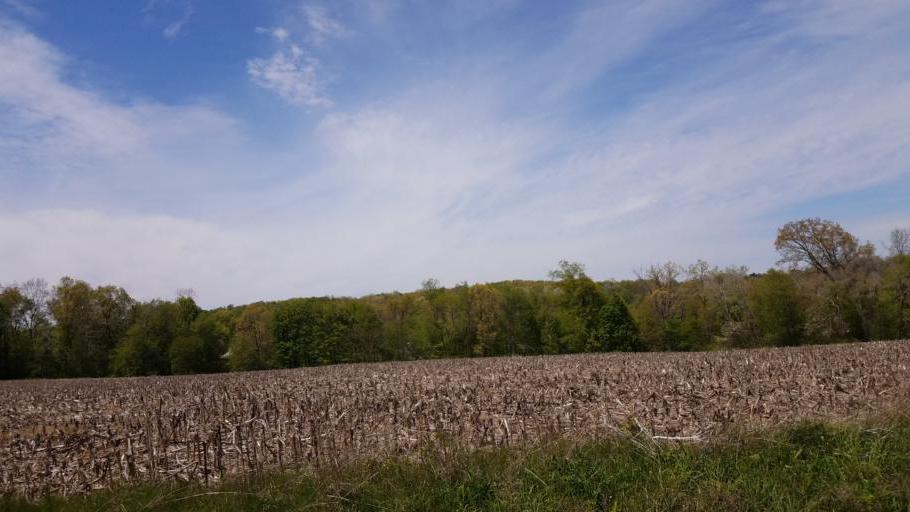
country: US
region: Ohio
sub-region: Knox County
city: Gambier
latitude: 40.4207
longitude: -82.3956
